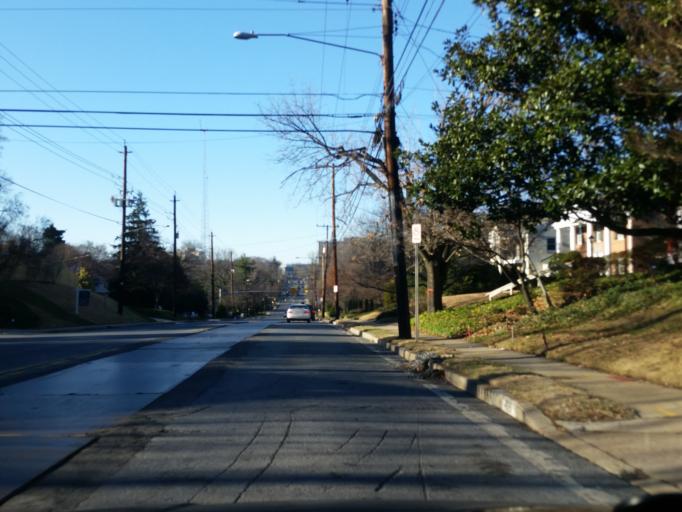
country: US
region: Maryland
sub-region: Montgomery County
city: Friendship Village
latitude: 38.9586
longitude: -77.0942
